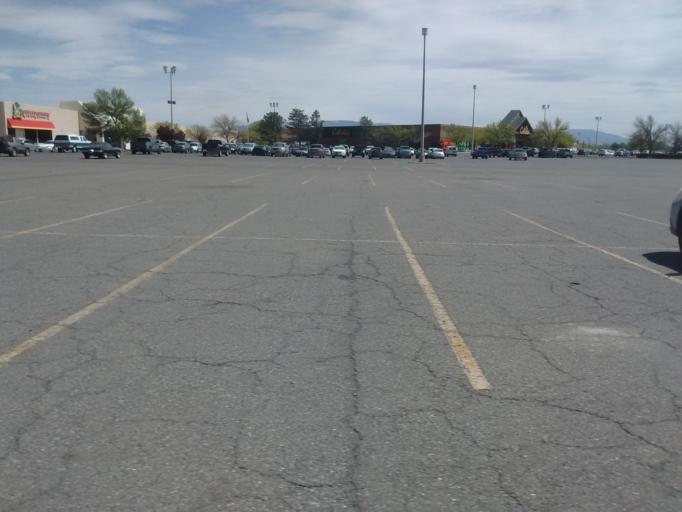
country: US
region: Colorado
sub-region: Mesa County
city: Redlands
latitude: 39.0915
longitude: -108.6049
